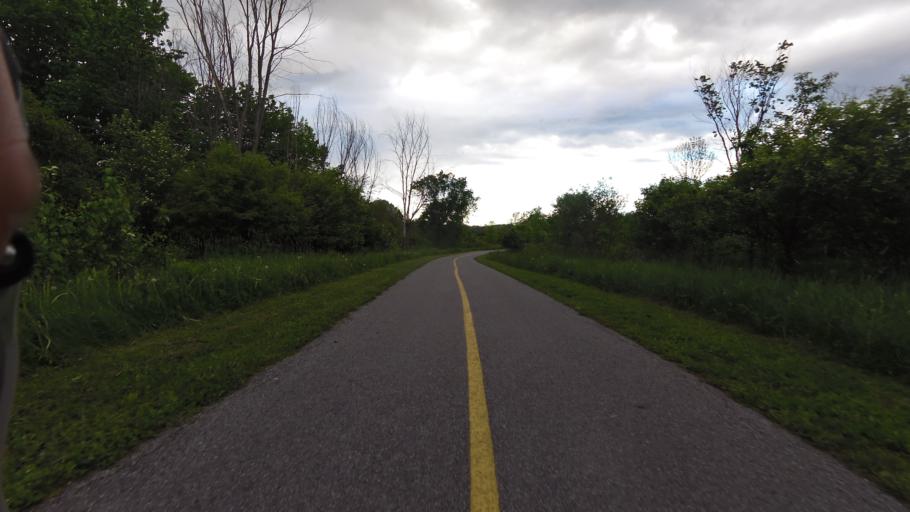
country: CA
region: Ontario
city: Bells Corners
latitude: 45.3340
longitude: -75.8866
